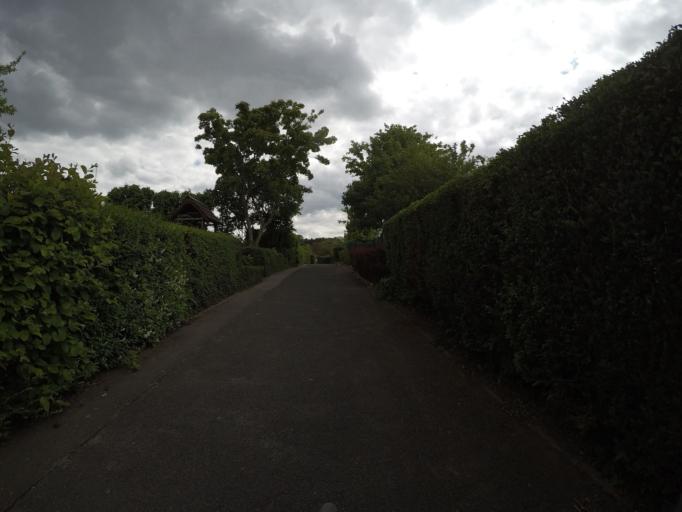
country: DE
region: Berlin
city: Schoneberg Bezirk
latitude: 52.4629
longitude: 13.3511
